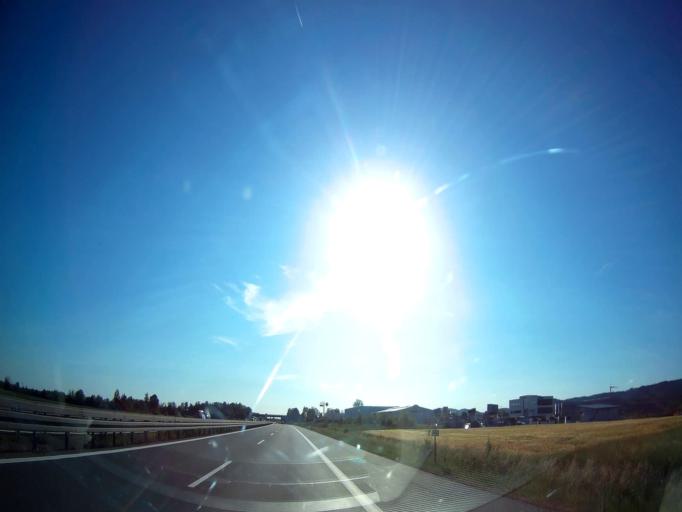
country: DE
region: Bavaria
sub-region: Upper Palatinate
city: Wiesent
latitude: 49.0008
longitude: 12.3707
